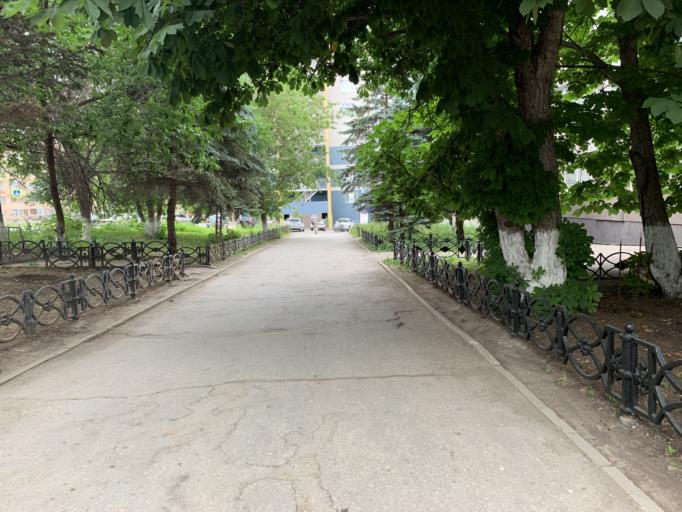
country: RU
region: Samara
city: Samara
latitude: 53.2133
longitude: 50.1691
